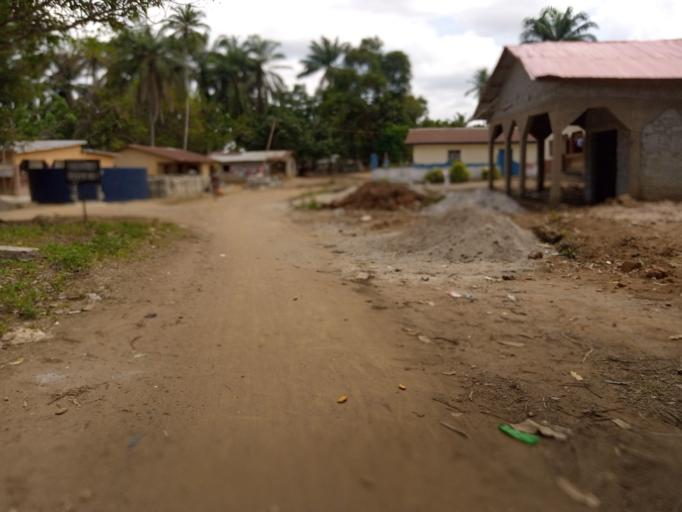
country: SL
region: Western Area
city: Waterloo
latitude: 8.3251
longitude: -13.0131
